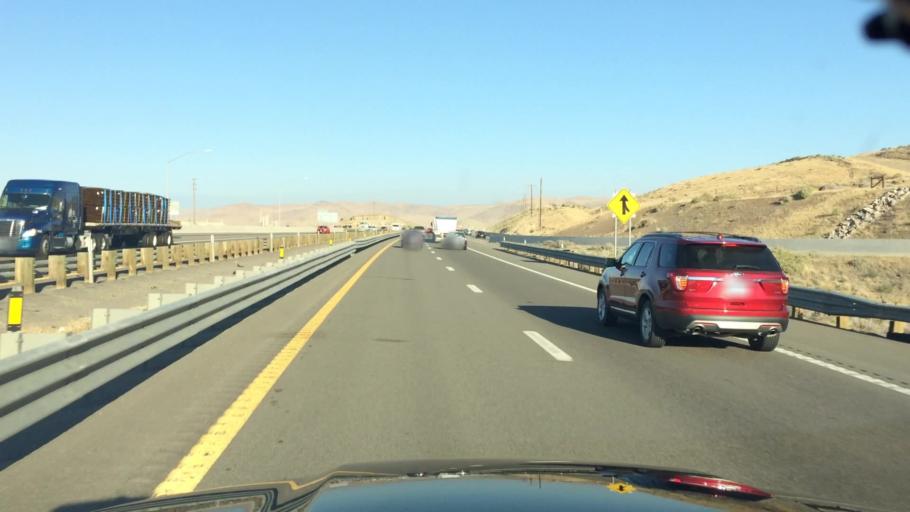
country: US
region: Nevada
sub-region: Lyon County
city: Stagecoach
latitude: 39.5664
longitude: -119.4890
